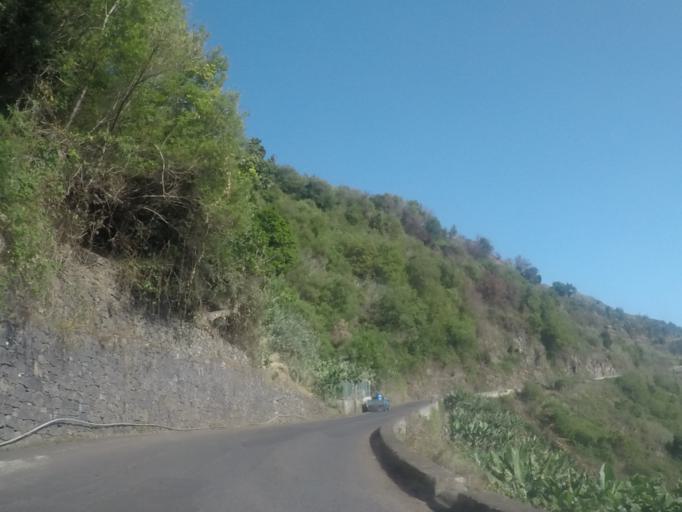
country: PT
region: Madeira
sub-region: Calheta
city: Arco da Calheta
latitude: 32.7130
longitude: -17.1308
